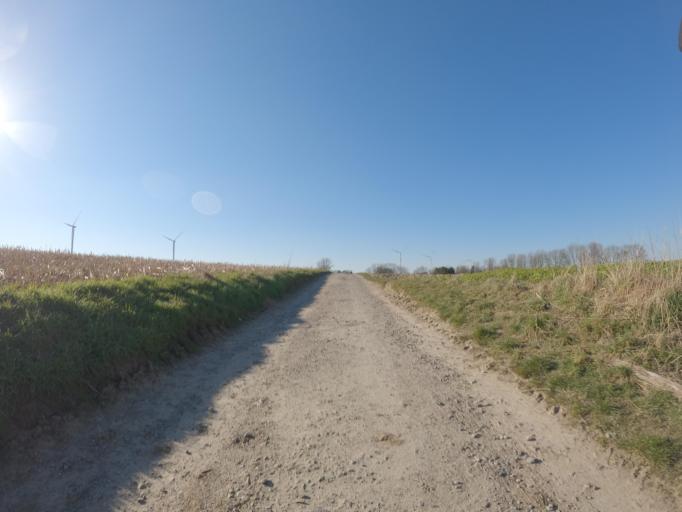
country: NL
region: Limburg
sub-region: Gemeente Kerkrade
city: Kerkrade
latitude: 50.8254
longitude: 6.0413
